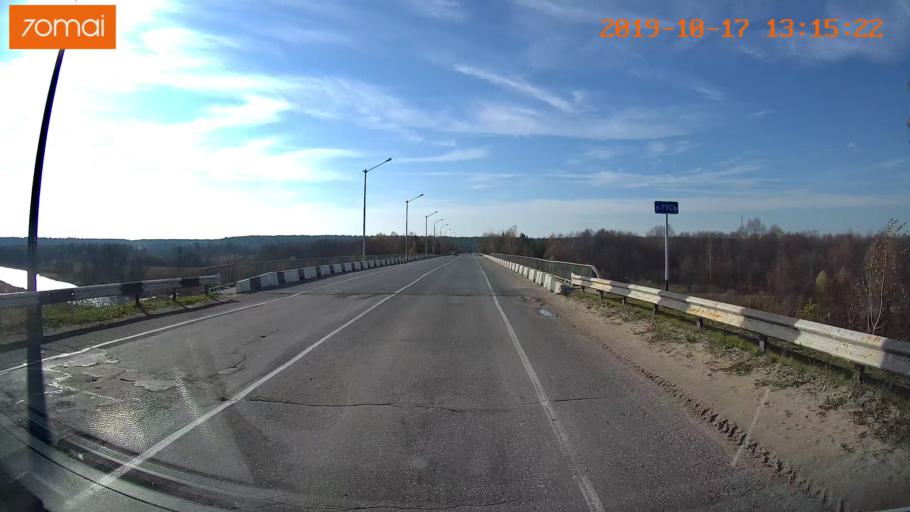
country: RU
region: Rjazan
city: Gus'-Zheleznyy
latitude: 55.0521
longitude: 41.1570
